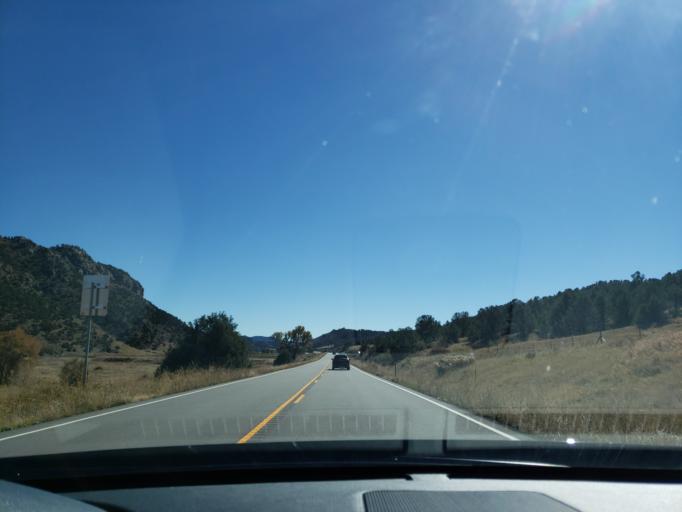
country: US
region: Colorado
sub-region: Fremont County
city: Canon City
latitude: 38.6146
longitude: -105.4441
